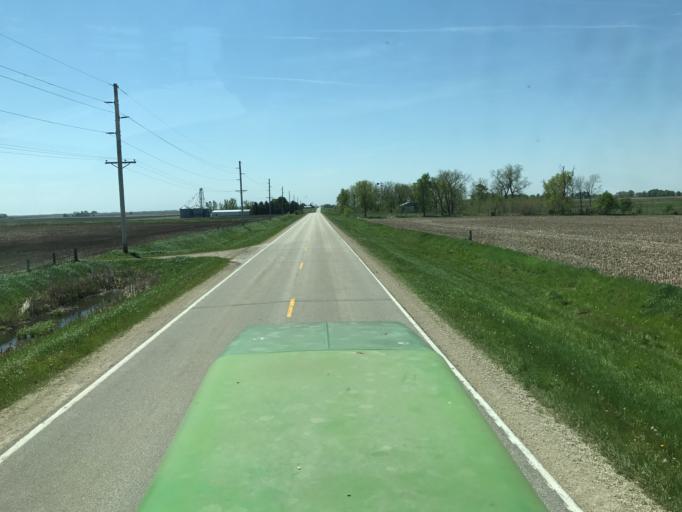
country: US
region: Iowa
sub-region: Butler County
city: Shell Rock
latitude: 42.6768
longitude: -92.5936
